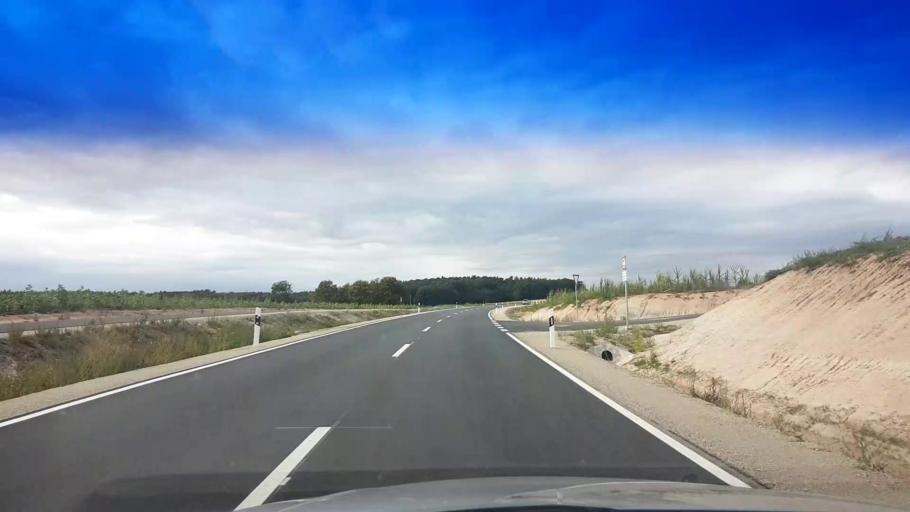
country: DE
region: Bavaria
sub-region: Upper Franconia
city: Frensdorf
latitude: 49.7952
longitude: 10.8807
